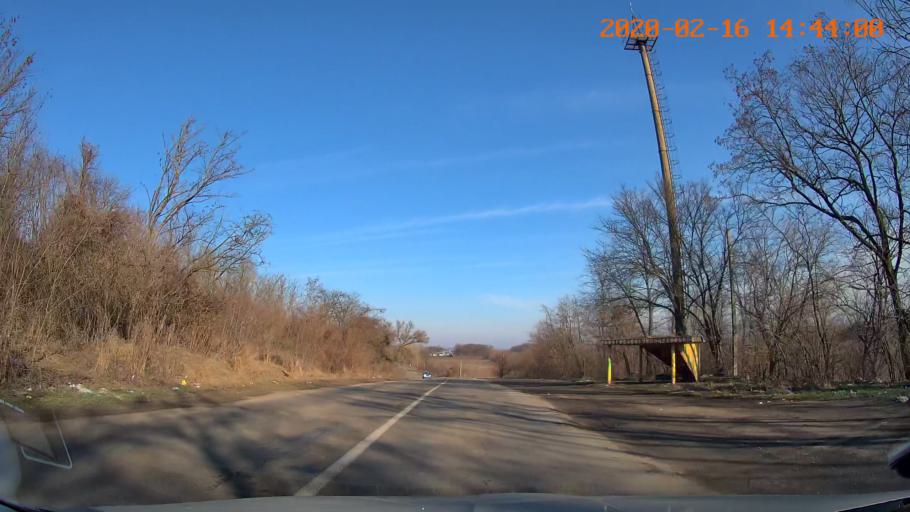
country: RO
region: Botosani
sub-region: Comuna Paltinis
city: Paltinis
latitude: 48.2604
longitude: 26.6083
